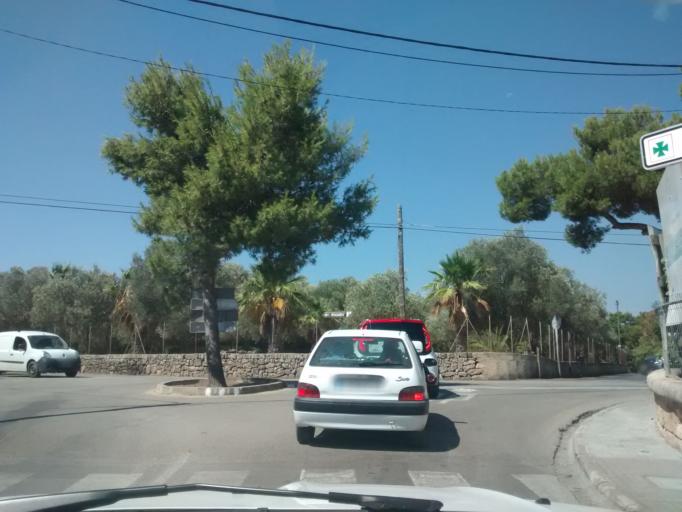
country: ES
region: Balearic Islands
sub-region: Illes Balears
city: Alcudia
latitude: 39.8618
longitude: 3.1402
